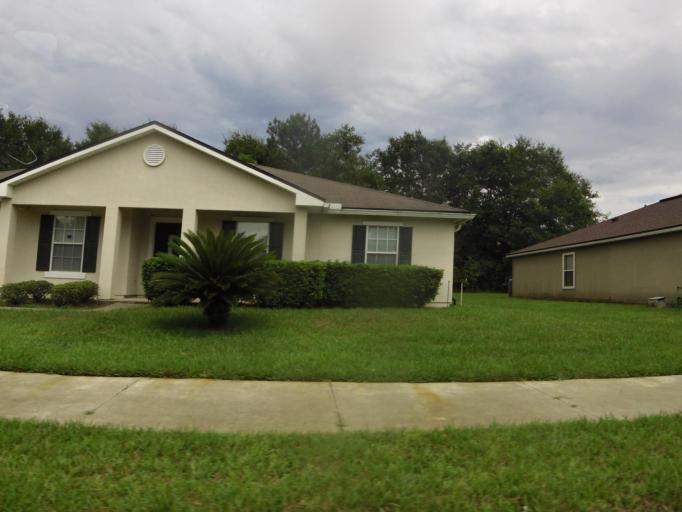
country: US
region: Florida
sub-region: Nassau County
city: Nassau Village-Ratliff
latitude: 30.4416
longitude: -81.7528
